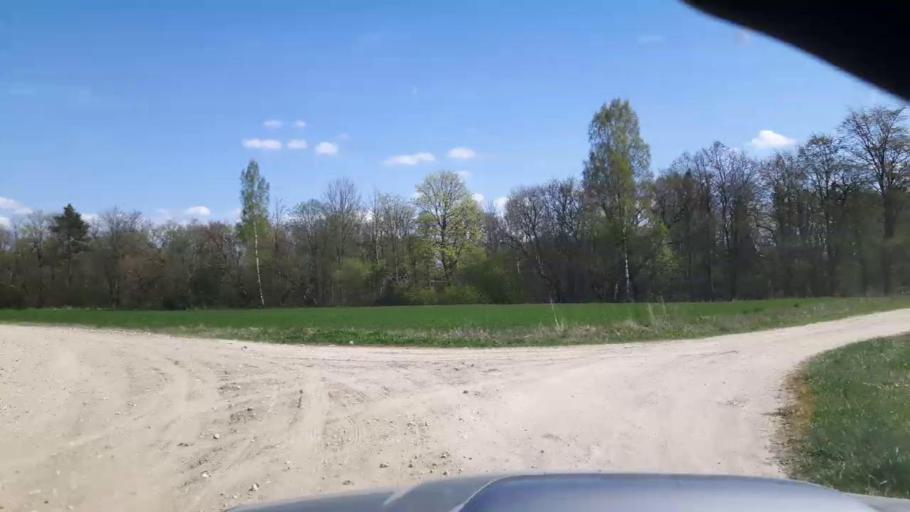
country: EE
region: Paernumaa
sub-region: Tootsi vald
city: Tootsi
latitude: 58.4959
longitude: 24.9000
